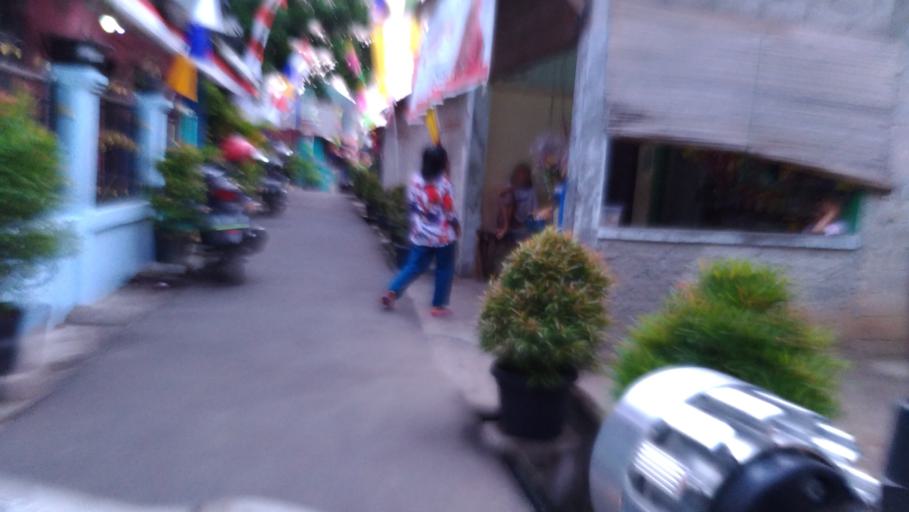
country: ID
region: West Java
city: Depok
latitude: -6.3482
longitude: 106.8728
